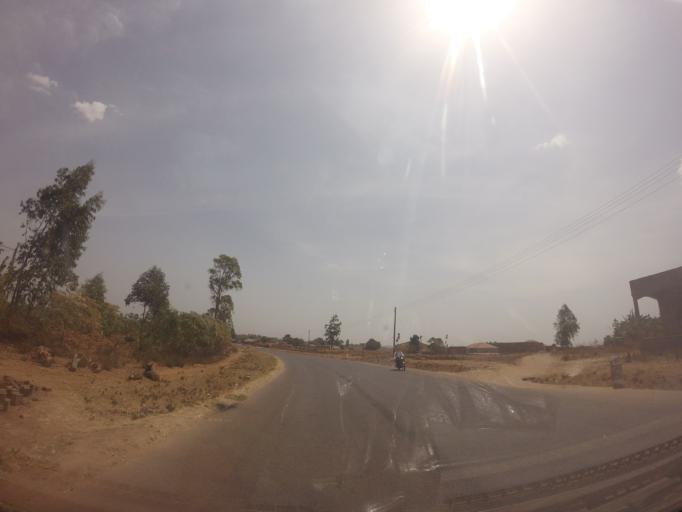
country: UG
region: Northern Region
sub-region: Arua District
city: Arua
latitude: 2.9545
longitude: 30.9184
